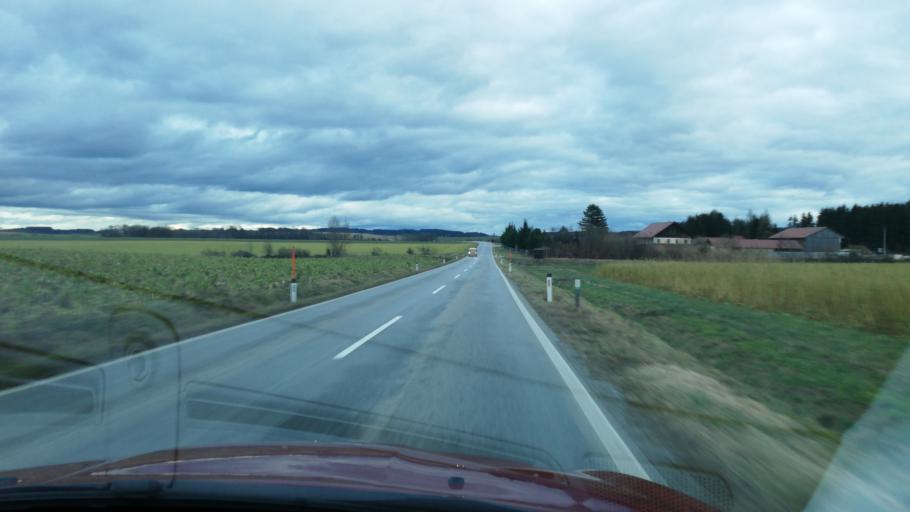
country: DE
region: Bavaria
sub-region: Lower Bavaria
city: Bad Fussing
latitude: 48.2654
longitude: 13.3189
